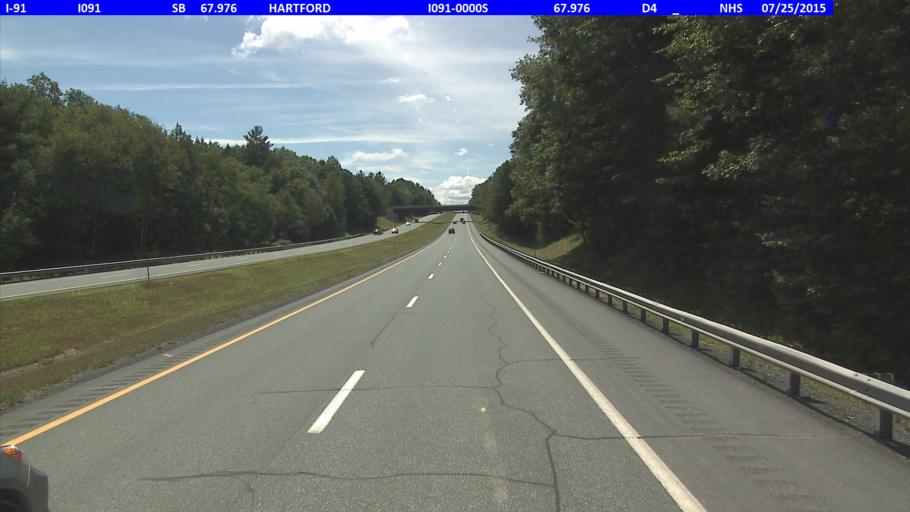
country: US
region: Vermont
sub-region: Windsor County
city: White River Junction
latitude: 43.6149
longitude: -72.3470
